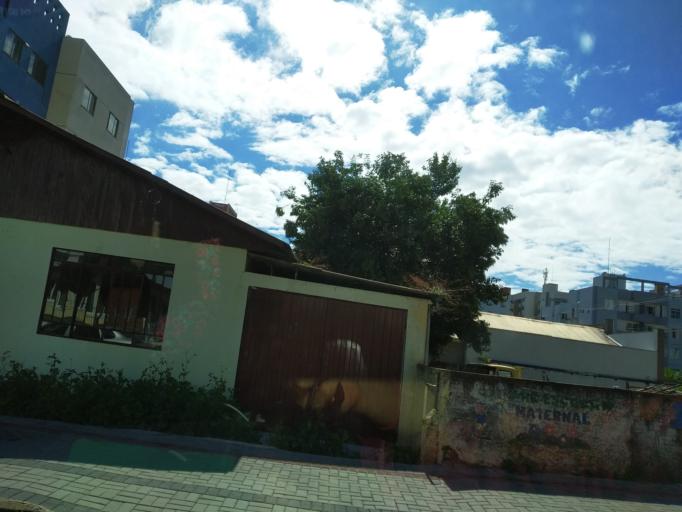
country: BR
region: Parana
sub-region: Pato Branco
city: Pato Branco
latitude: -26.2259
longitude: -52.6683
